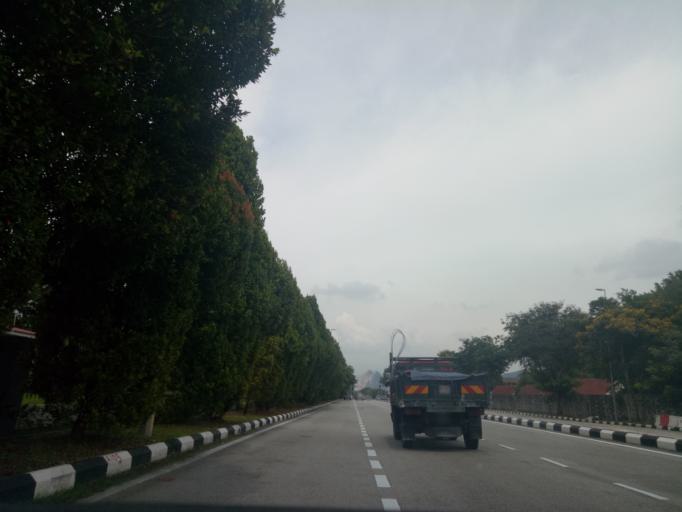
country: MY
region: Perak
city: Ipoh
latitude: 4.5941
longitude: 101.1214
